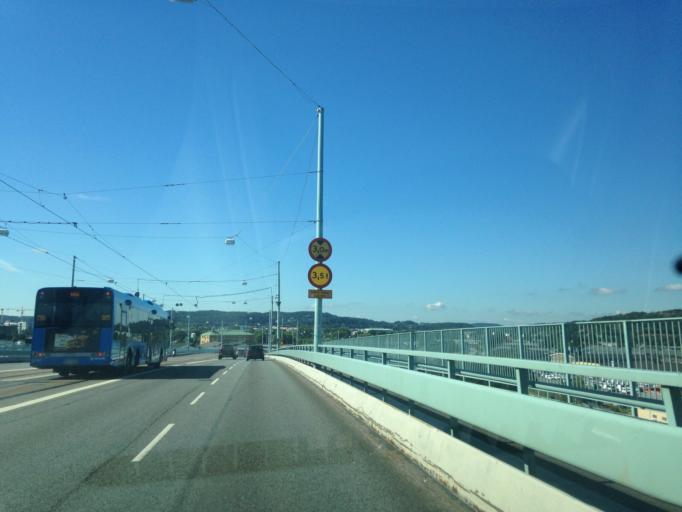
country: SE
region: Vaestra Goetaland
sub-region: Goteborg
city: Goeteborg
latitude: 57.7148
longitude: 11.9670
